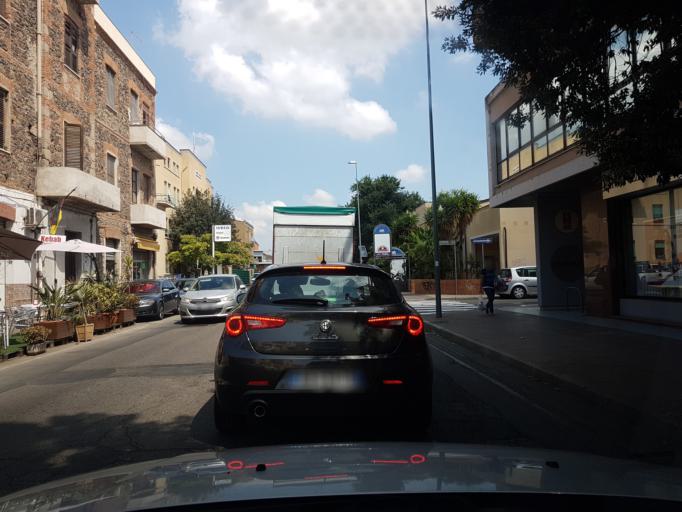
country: IT
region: Sardinia
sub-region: Provincia di Oristano
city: Oristano
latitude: 39.9066
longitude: 8.5884
